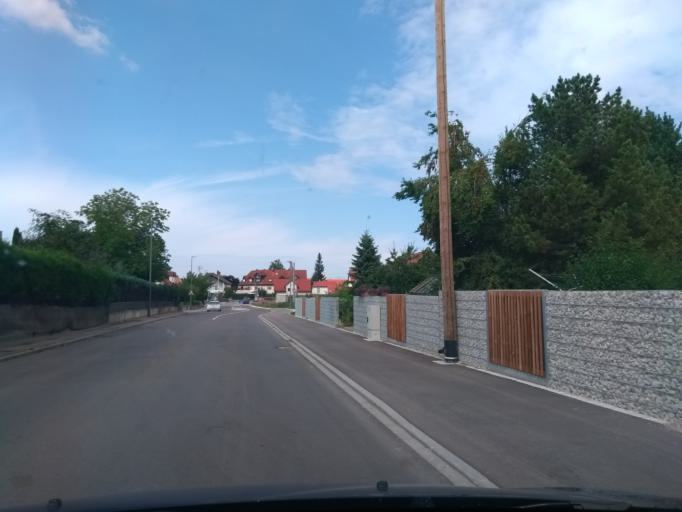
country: DE
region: Bavaria
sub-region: Upper Bavaria
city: Markt Indersdorf
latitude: 48.3508
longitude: 11.3831
